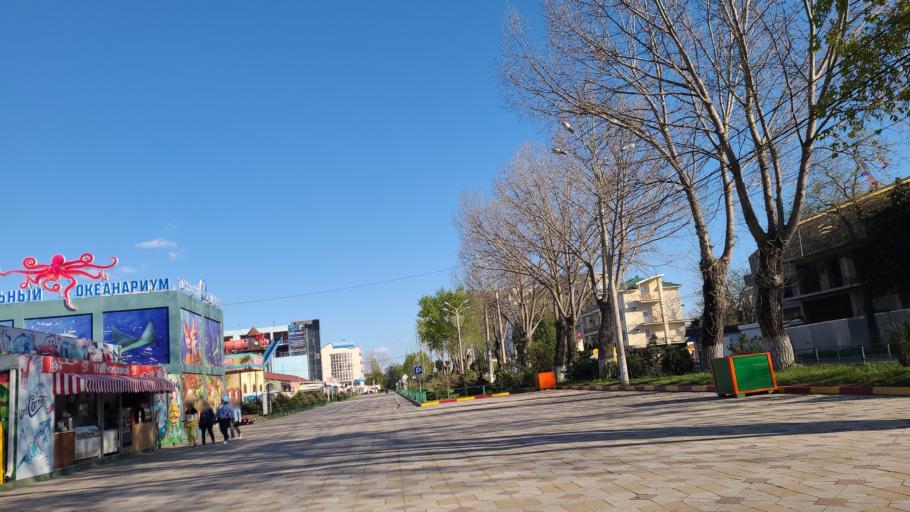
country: RU
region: Krasnodarskiy
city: Tsibanobalka
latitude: 44.9451
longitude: 37.3045
